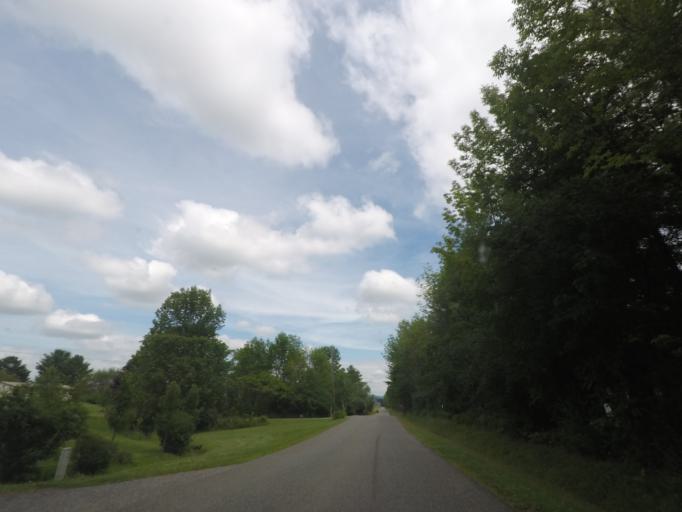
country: US
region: New York
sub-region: Saratoga County
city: Stillwater
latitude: 43.0119
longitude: -73.6408
